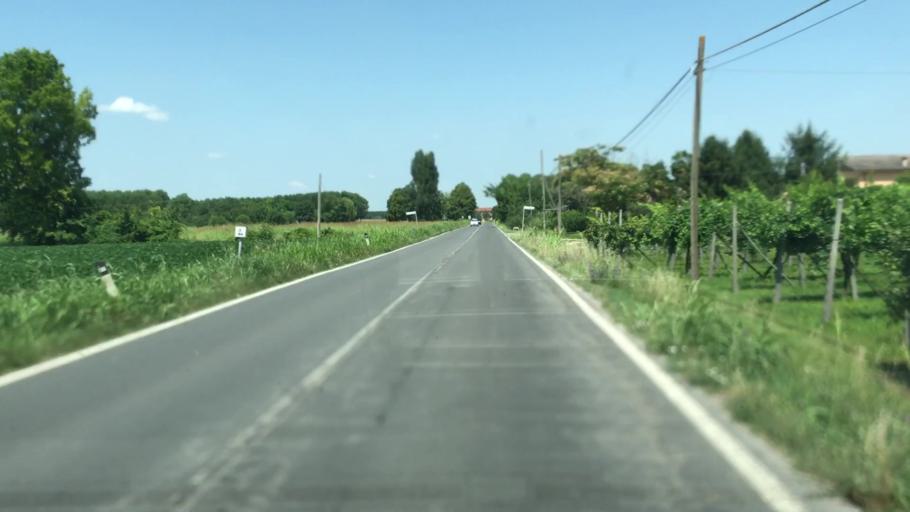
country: IT
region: Veneto
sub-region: Provincia di Rovigo
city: Castelnovo Bariano
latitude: 45.0415
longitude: 11.2897
